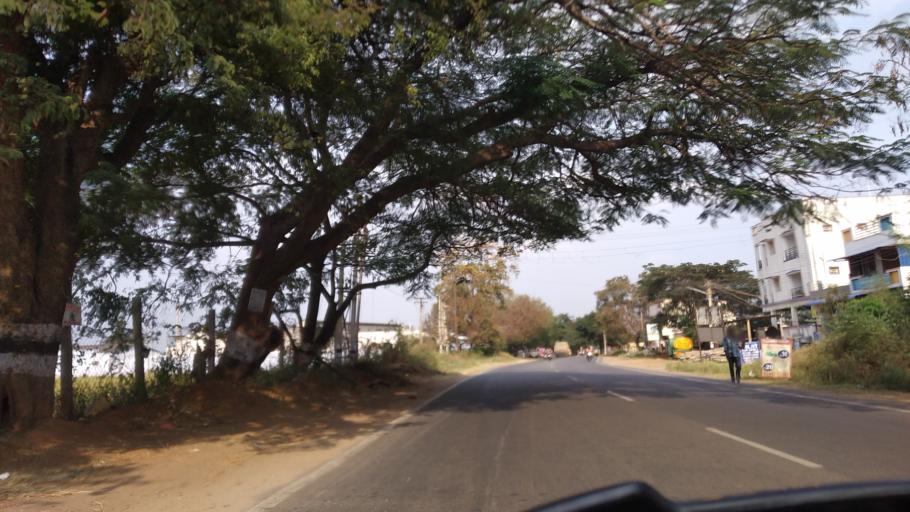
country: IN
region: Tamil Nadu
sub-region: Coimbatore
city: Perur
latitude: 10.9683
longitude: 76.9053
